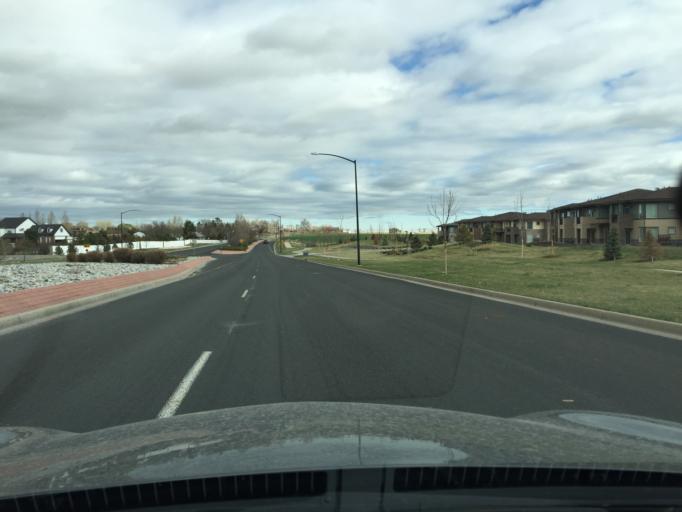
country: US
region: Colorado
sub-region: Adams County
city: Northglenn
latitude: 39.9655
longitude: -104.9966
